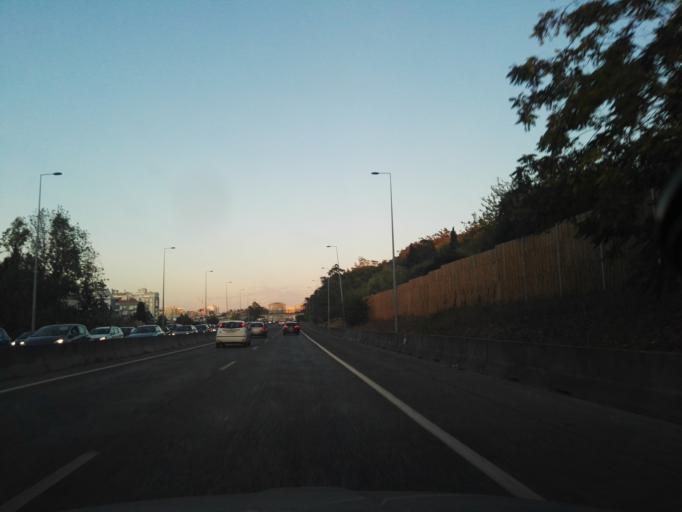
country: PT
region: Lisbon
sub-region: Odivelas
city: Pontinha
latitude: 38.7436
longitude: -9.1943
